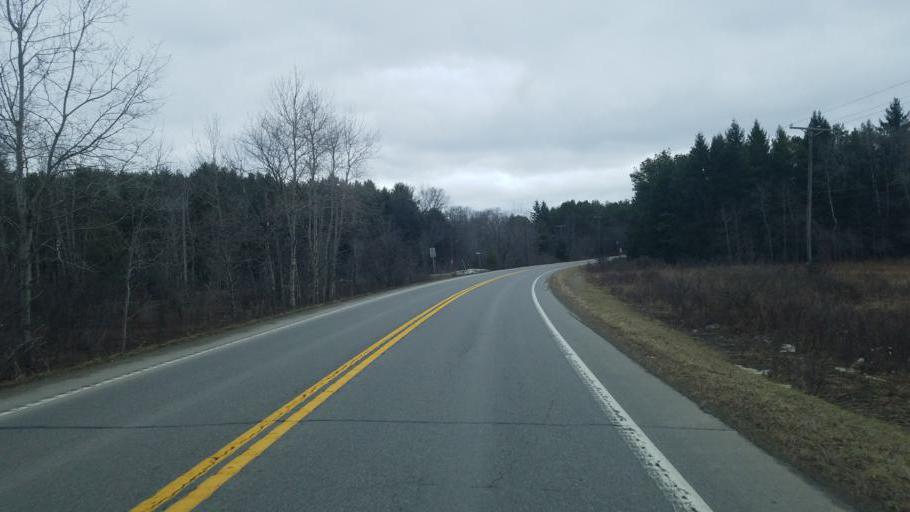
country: US
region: Pennsylvania
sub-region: Forest County
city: Marienville
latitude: 41.4357
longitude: -79.1861
